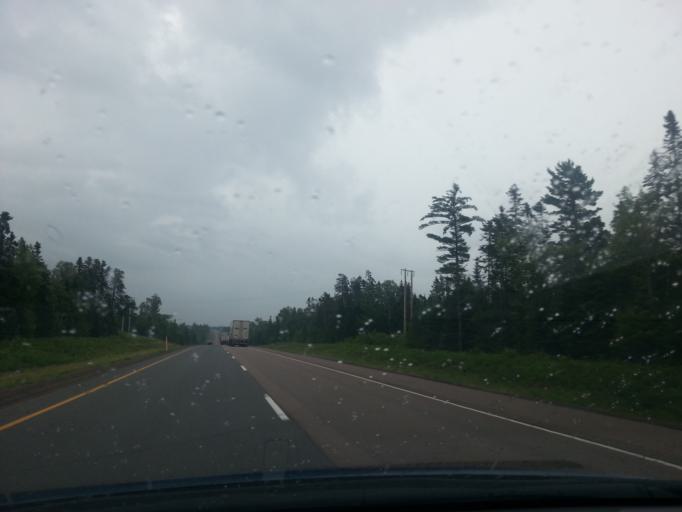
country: CA
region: New Brunswick
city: Hampton
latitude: 45.8465
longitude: -66.0667
